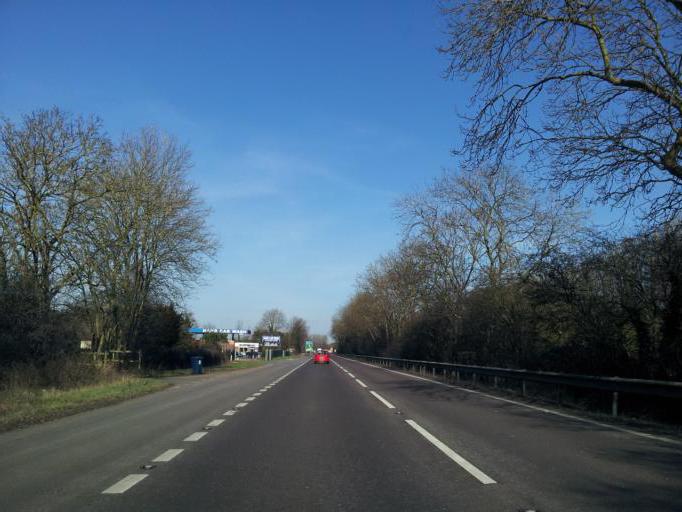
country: GB
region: England
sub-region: Cambridgeshire
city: Little Paxton
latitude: 52.2580
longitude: -0.2638
